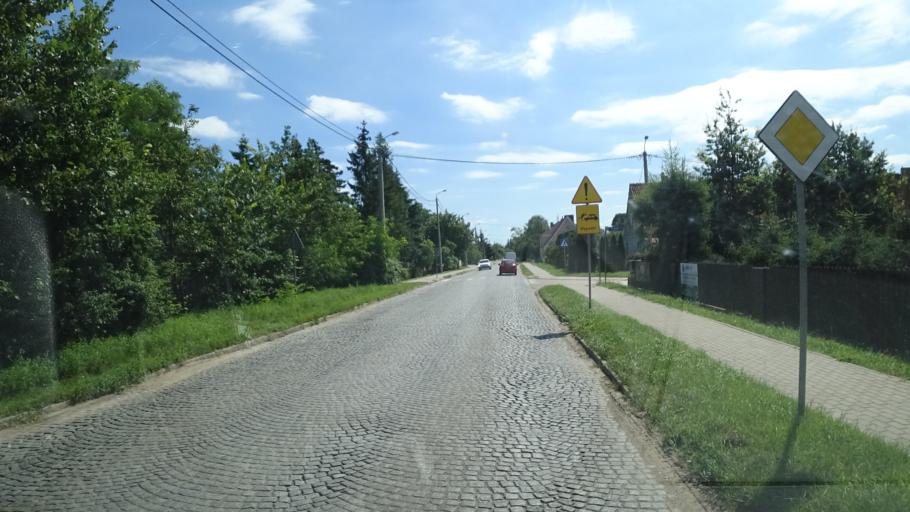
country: PL
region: Warmian-Masurian Voivodeship
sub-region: Powiat elcki
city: Prostki
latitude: 53.6922
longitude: 22.4438
